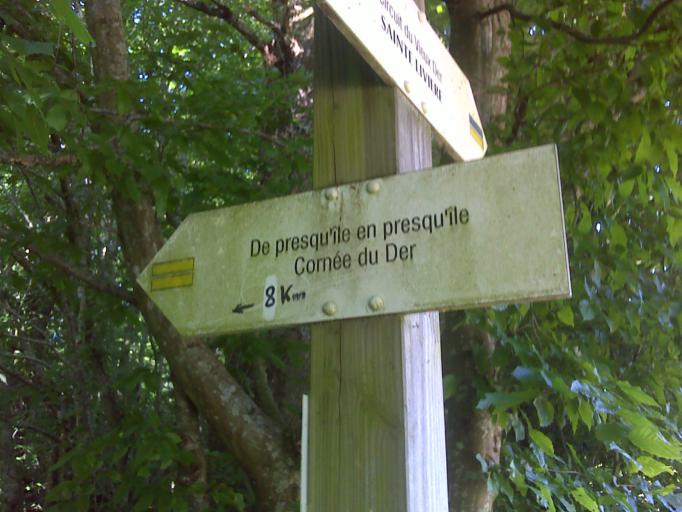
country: FR
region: Champagne-Ardenne
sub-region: Departement de la Haute-Marne
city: Villiers-en-Lieu
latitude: 48.5772
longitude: 4.8464
